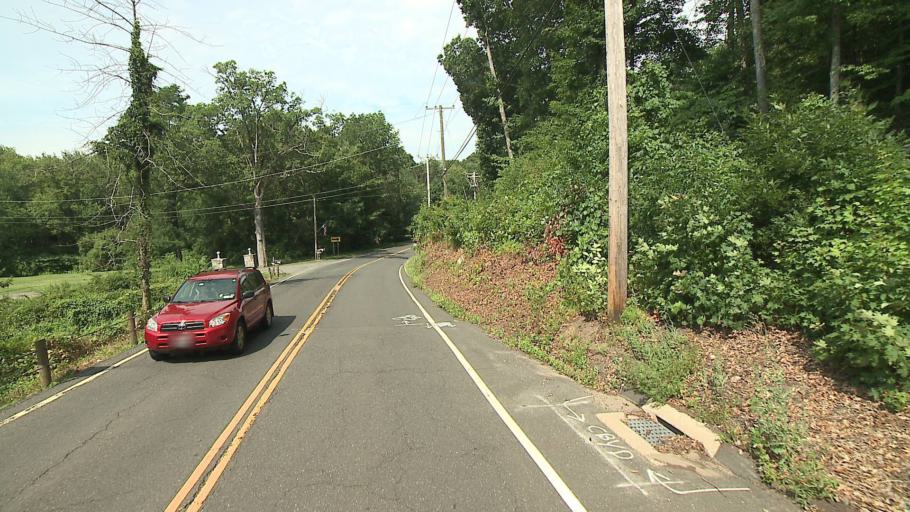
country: US
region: New York
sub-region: Putnam County
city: Putnam Lake
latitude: 41.4440
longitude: -73.5204
